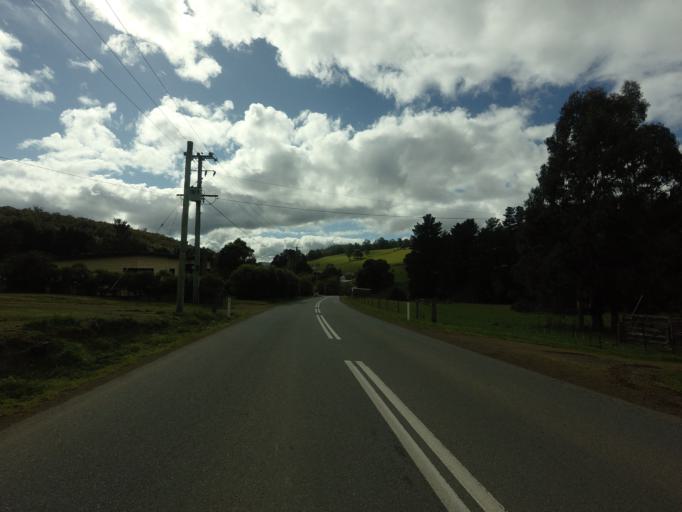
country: AU
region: Tasmania
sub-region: Huon Valley
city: Geeveston
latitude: -43.2414
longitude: 146.9919
